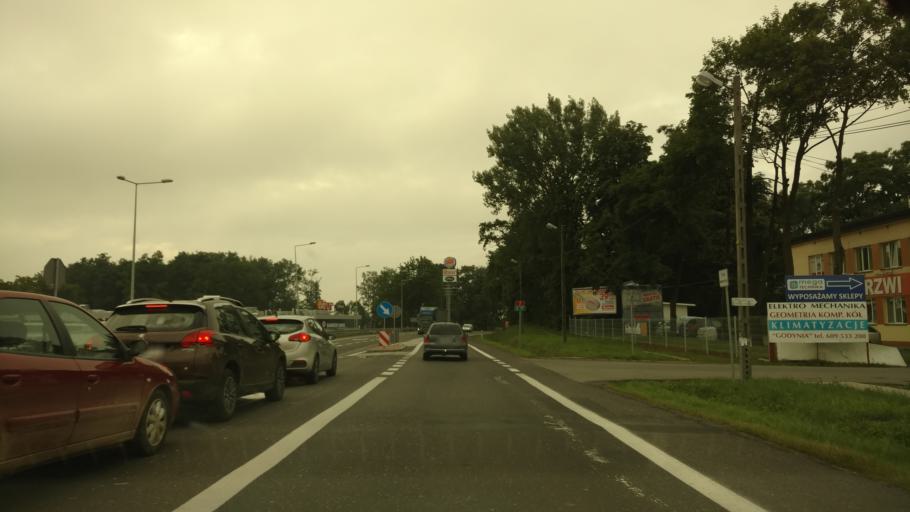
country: PL
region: Lesser Poland Voivodeship
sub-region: Powiat krakowski
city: Michalowice
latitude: 50.1172
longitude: 19.9670
